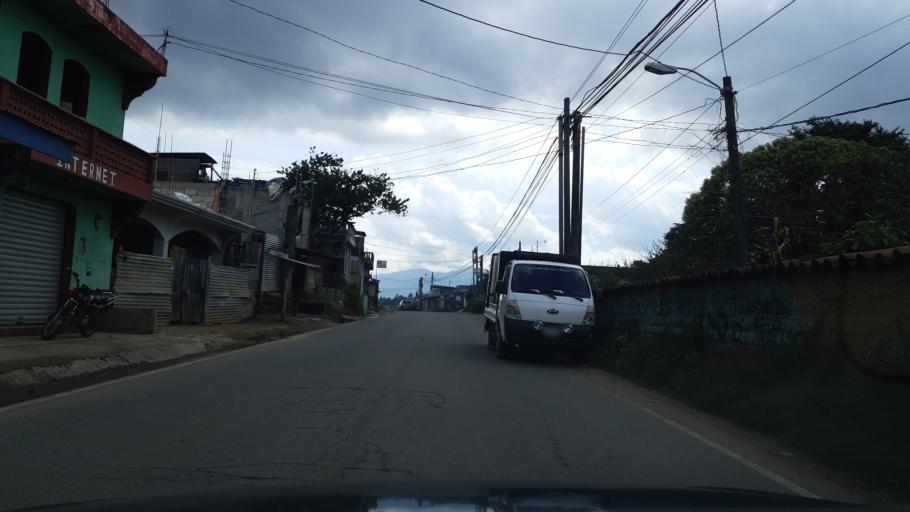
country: GT
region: Chimaltenango
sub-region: Municipio de Chimaltenango
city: Chimaltenango
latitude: 14.6827
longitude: -90.7981
